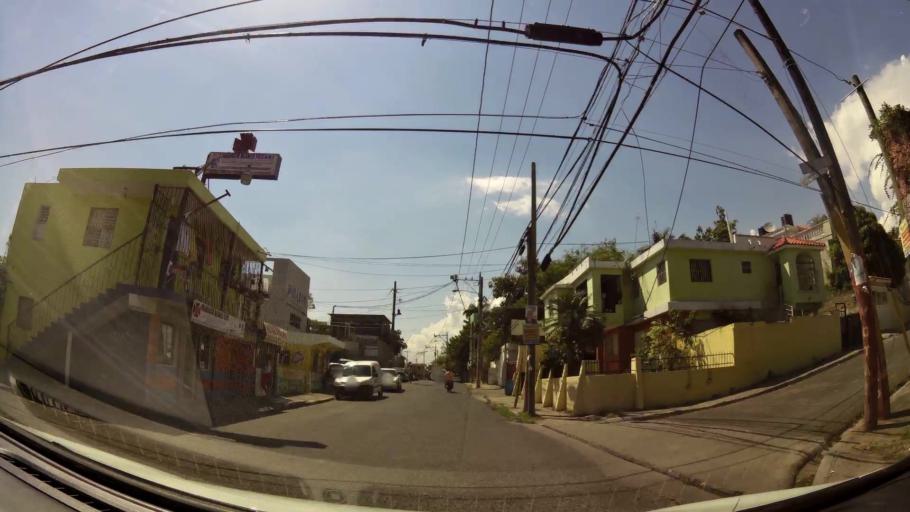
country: DO
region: Nacional
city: Bella Vista
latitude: 18.4643
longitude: -69.9778
